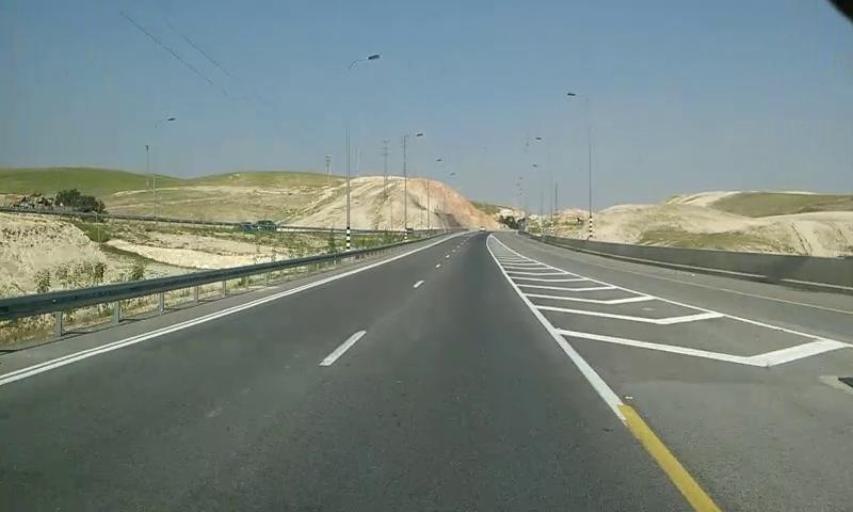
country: PS
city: Az Za`ayyim
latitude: 31.8112
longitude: 35.3406
